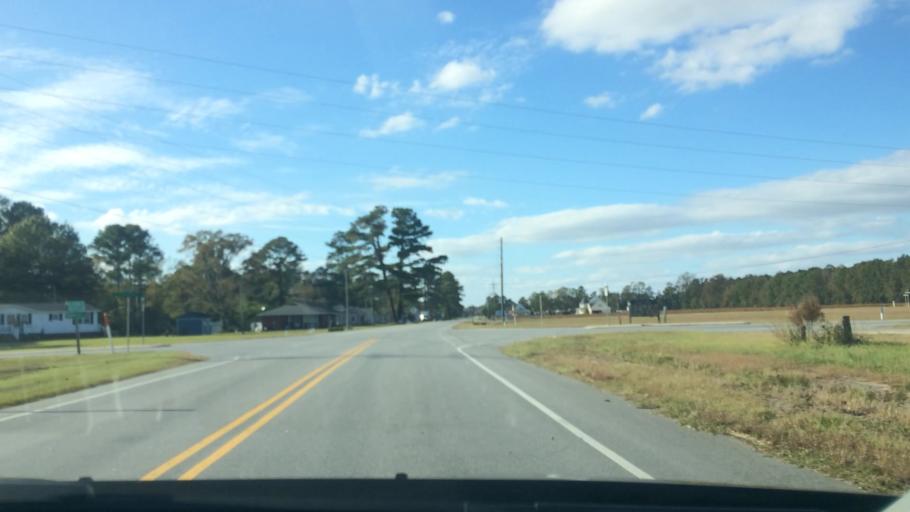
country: US
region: North Carolina
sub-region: Greene County
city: Maury
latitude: 35.4708
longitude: -77.5456
